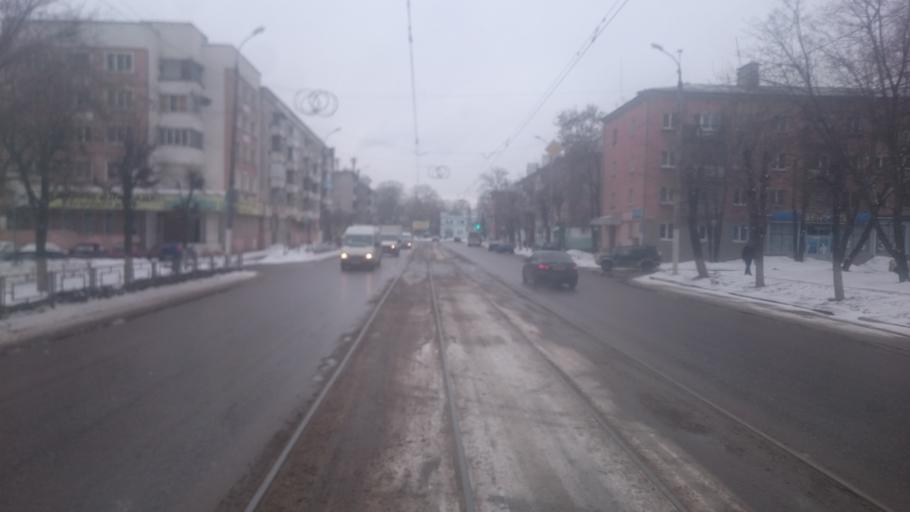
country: RU
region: Tverskaya
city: Tver
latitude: 56.8702
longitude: 35.8839
